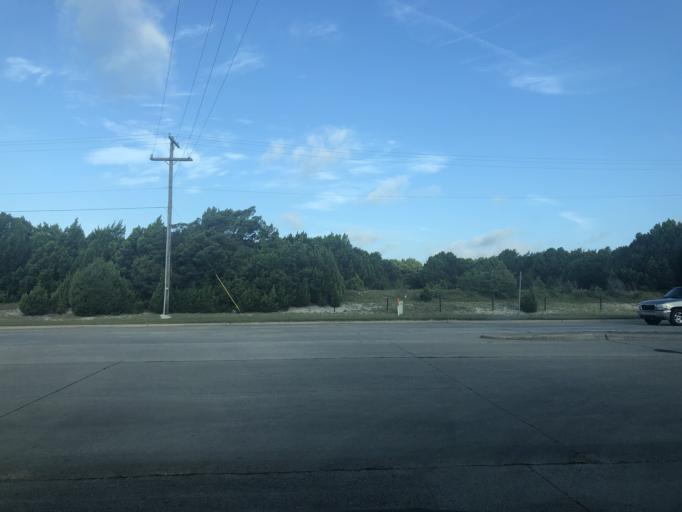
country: US
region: Texas
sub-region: Dallas County
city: Duncanville
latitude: 32.6639
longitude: -96.9429
